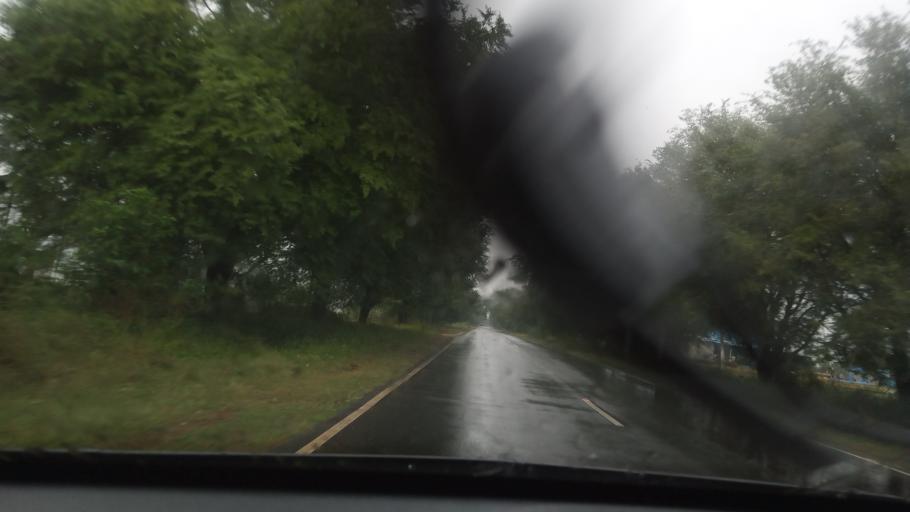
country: IN
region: Tamil Nadu
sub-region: Vellore
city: Kalavai
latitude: 12.8424
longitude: 79.4004
